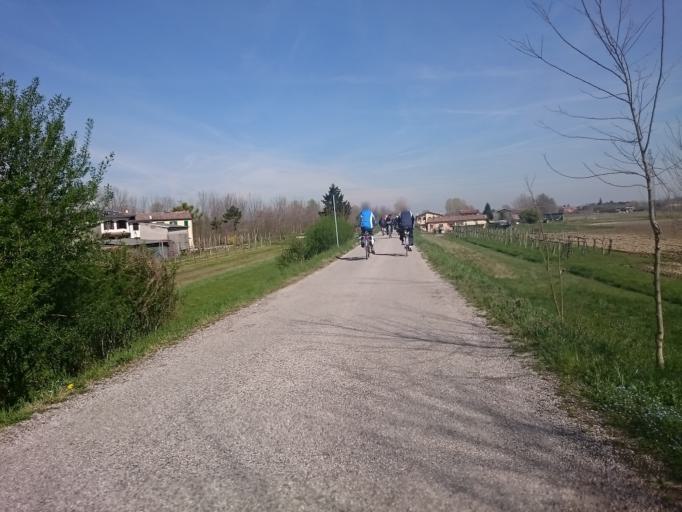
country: IT
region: Veneto
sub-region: Provincia di Padova
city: Sarmeola
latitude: 45.4282
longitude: 11.8292
